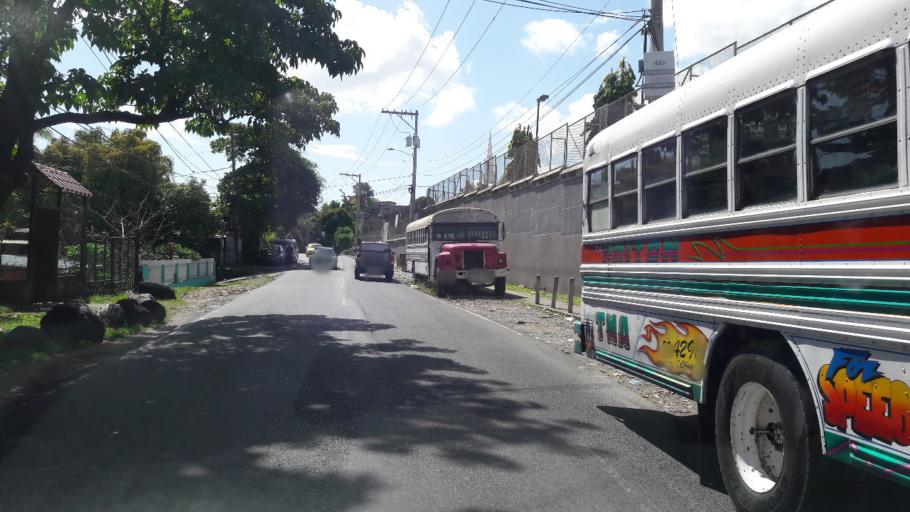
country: PA
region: Panama
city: San Miguelito
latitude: 9.0475
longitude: -79.5055
